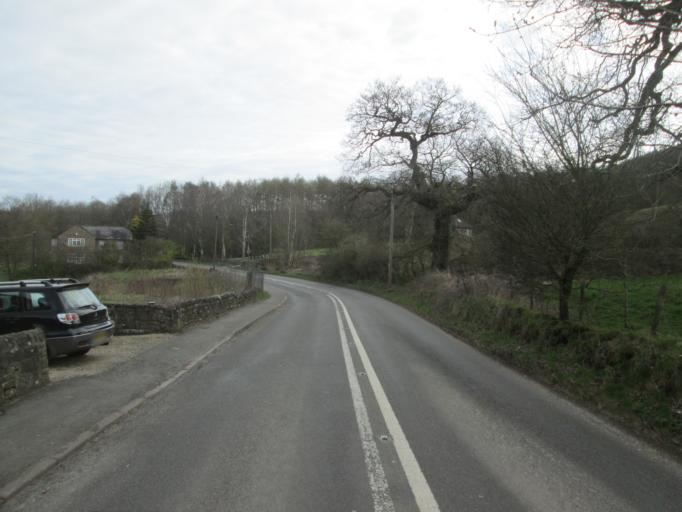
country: GB
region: England
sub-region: Derbyshire
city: Bakewell
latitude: 53.1954
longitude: -1.6096
